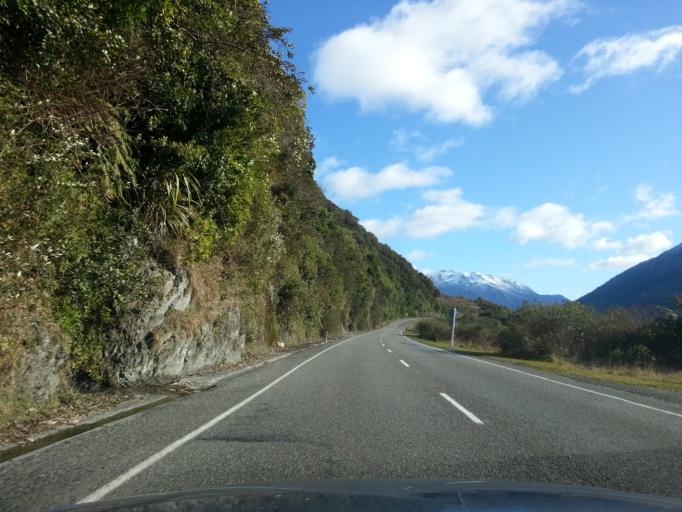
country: NZ
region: West Coast
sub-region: Grey District
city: Greymouth
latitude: -42.7338
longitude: 171.4459
